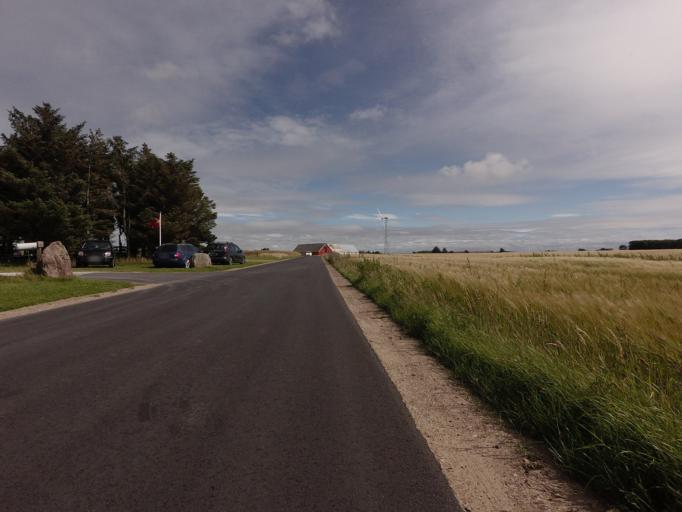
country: DK
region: North Denmark
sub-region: Hjorring Kommune
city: Vra
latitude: 57.3966
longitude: 9.7655
